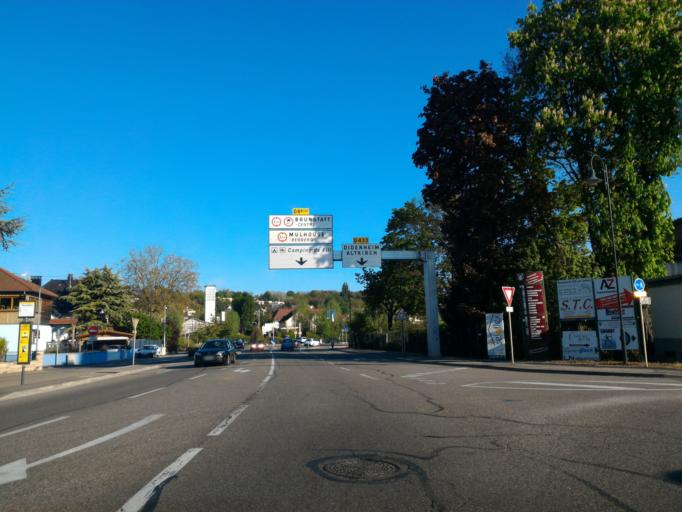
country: FR
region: Alsace
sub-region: Departement du Haut-Rhin
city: Brunstatt
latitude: 47.7305
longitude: 7.3202
